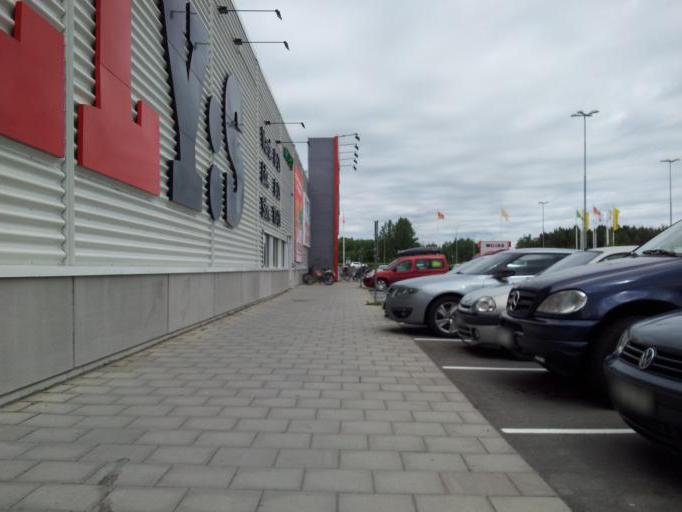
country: SE
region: Uppsala
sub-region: Uppsala Kommun
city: Gamla Uppsala
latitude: 59.8857
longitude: 17.6614
